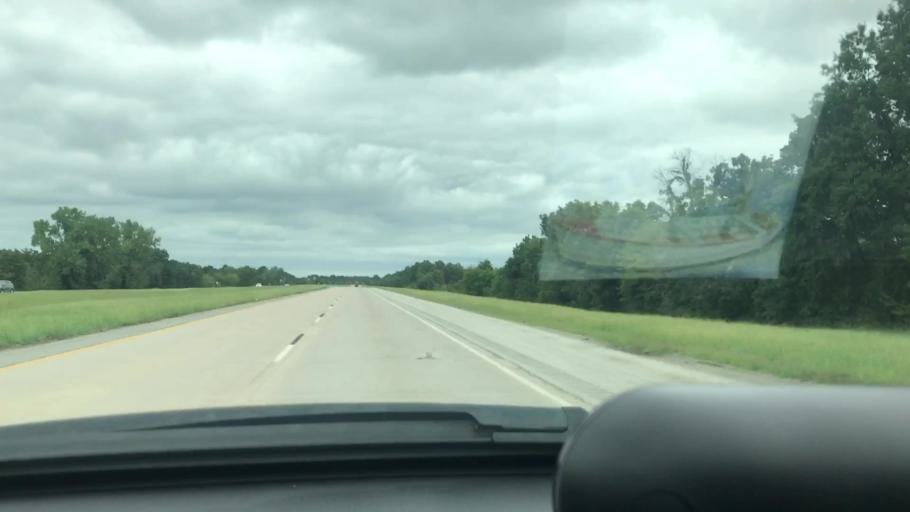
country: US
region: Oklahoma
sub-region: Wagoner County
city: Wagoner
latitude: 35.8979
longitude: -95.4026
